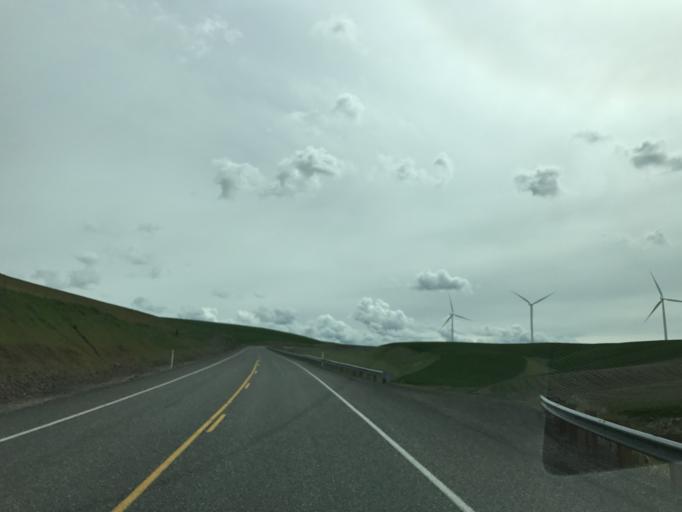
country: US
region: Washington
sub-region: Garfield County
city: Pomeroy
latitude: 46.5469
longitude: -117.7752
